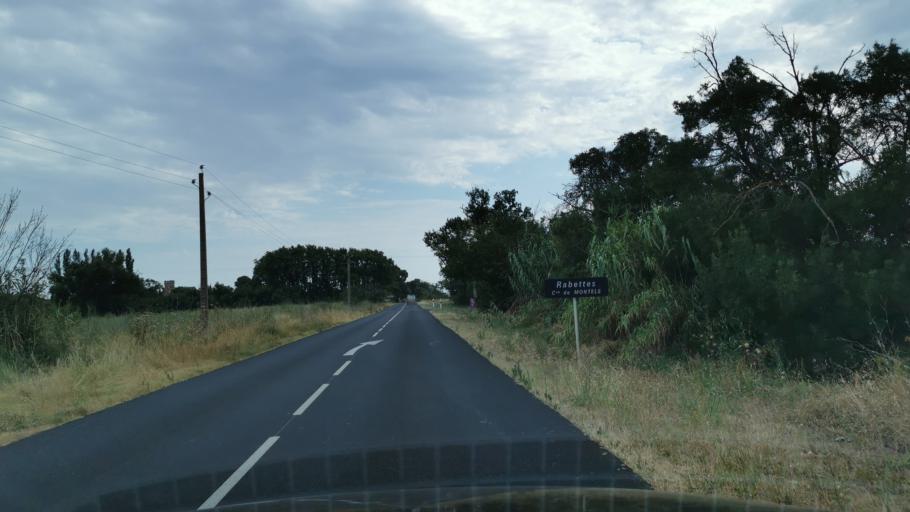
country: FR
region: Languedoc-Roussillon
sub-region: Departement de l'Aude
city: Ouveillan
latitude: 43.2799
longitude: 3.0183
